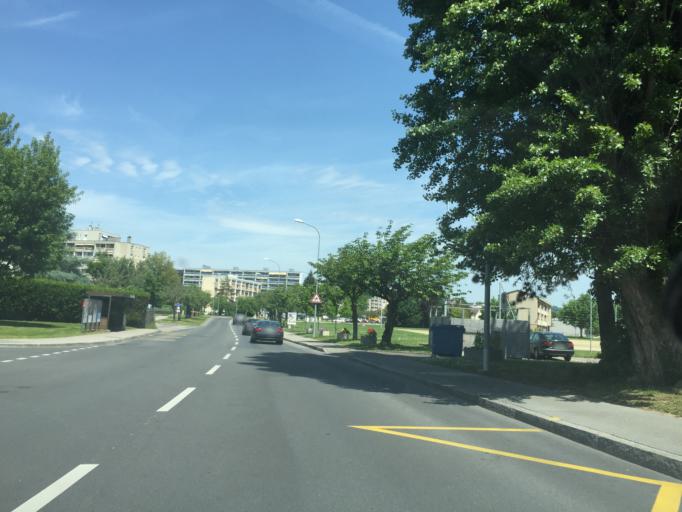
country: CH
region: Vaud
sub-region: Ouest Lausannois District
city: Ecublens
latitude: 46.5295
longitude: 6.5661
